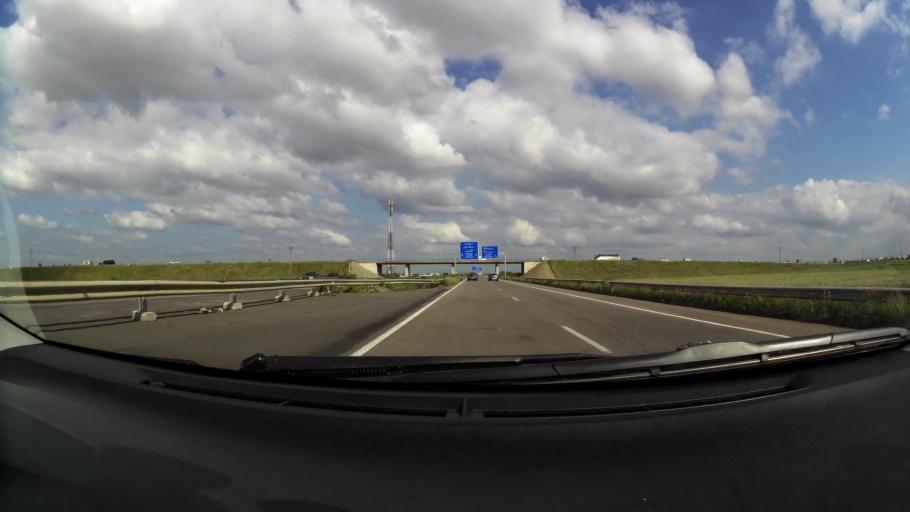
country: MA
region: Chaouia-Ouardigha
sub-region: Settat Province
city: Berrechid
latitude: 33.3023
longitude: -7.5747
